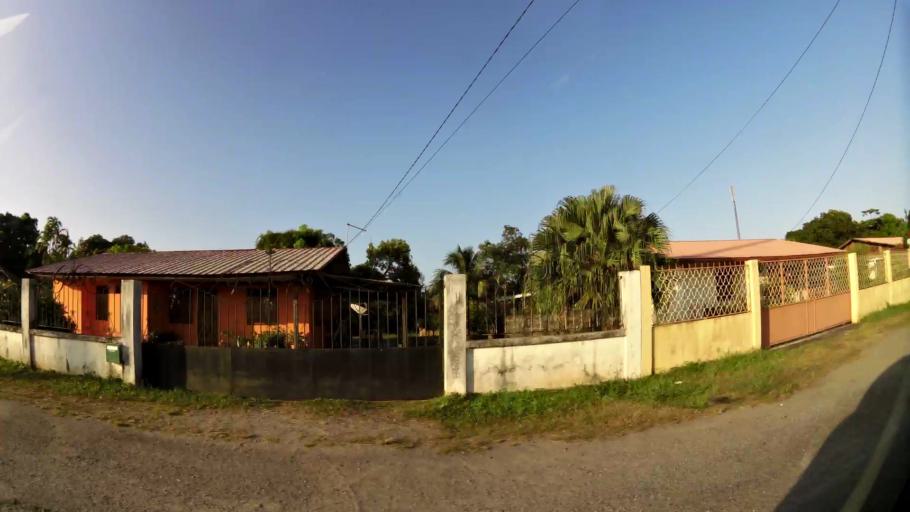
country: GF
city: Macouria
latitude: 5.0133
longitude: -52.4758
